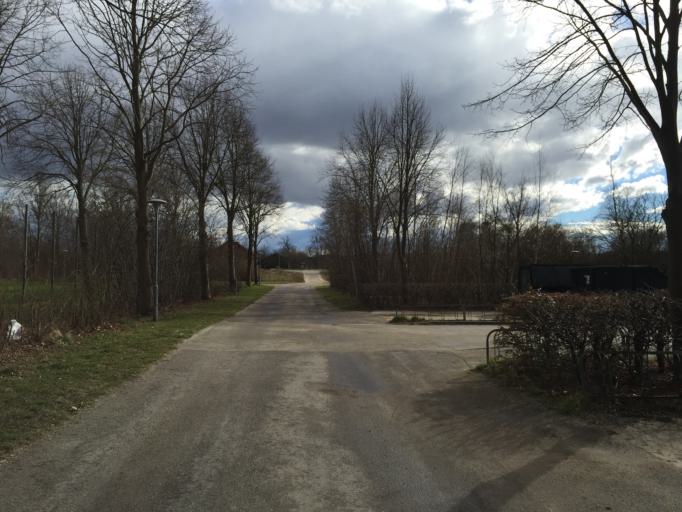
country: SE
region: Skane
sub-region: Lunds Kommun
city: Veberod
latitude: 55.6343
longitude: 13.4860
